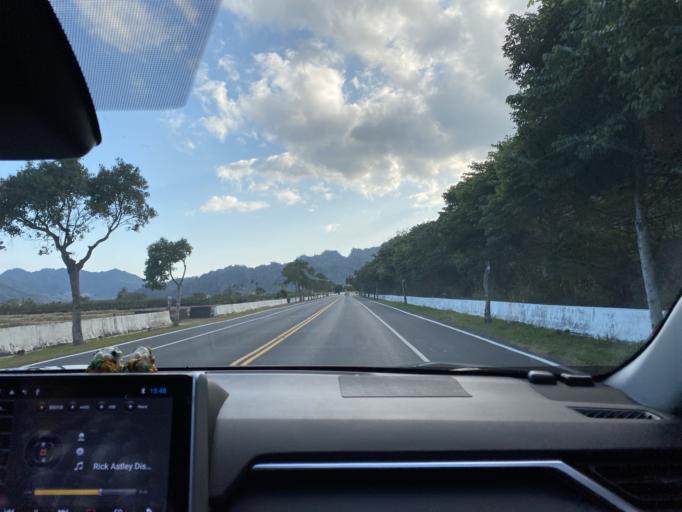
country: TW
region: Taiwan
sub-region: Taitung
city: Taitung
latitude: 22.8985
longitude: 121.1364
